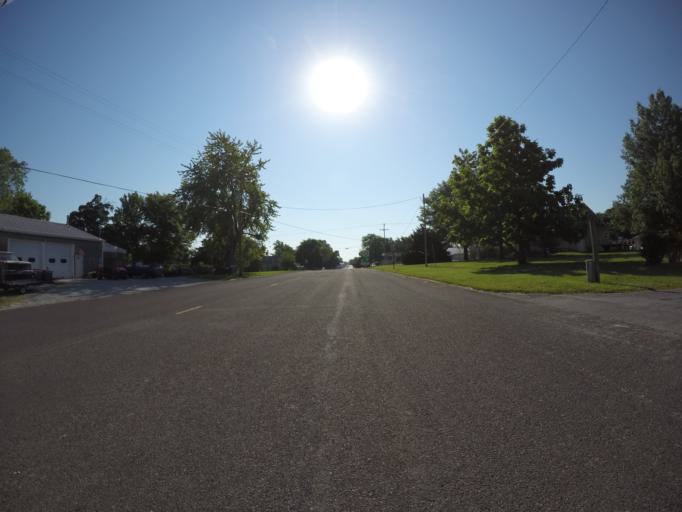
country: US
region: Kansas
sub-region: Brown County
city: Hiawatha
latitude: 39.8529
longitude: -95.5467
